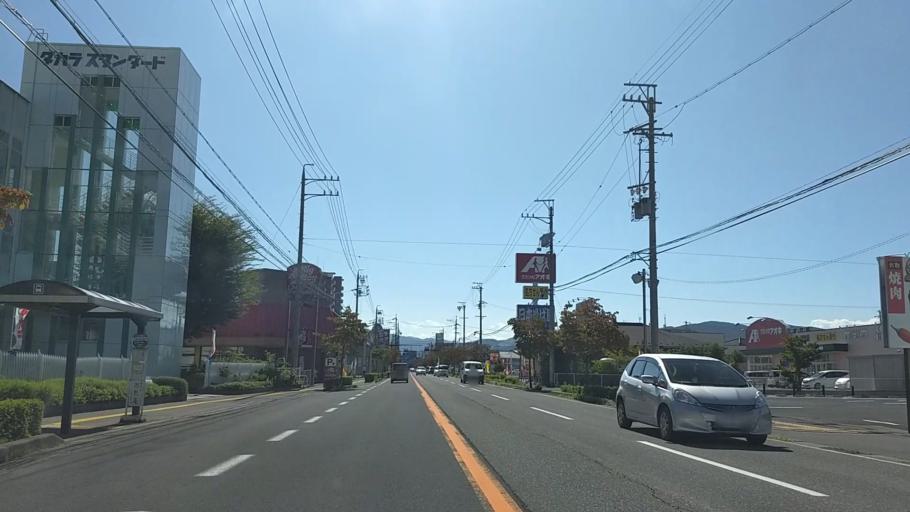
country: JP
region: Nagano
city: Nagano-shi
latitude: 36.6084
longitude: 138.1677
